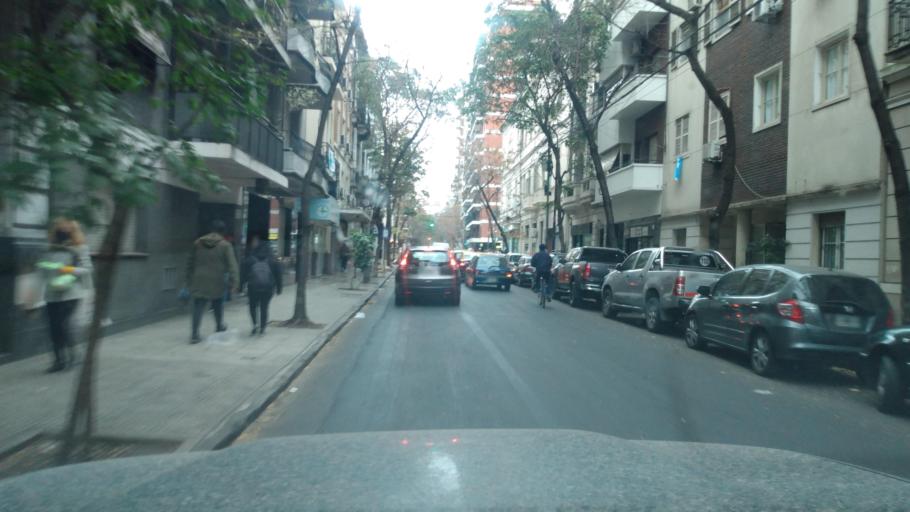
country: AR
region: Buenos Aires F.D.
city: Buenos Aires
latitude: -34.6086
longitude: -58.3965
